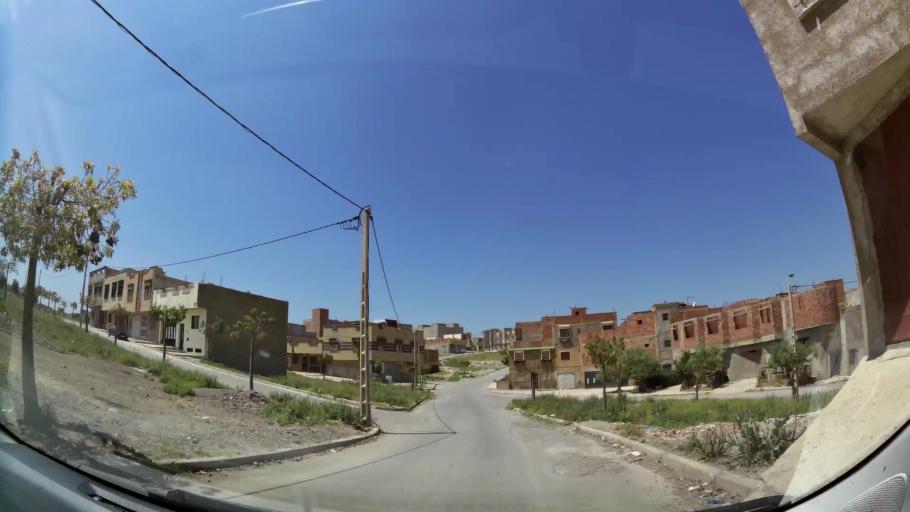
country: MA
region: Oriental
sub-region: Oujda-Angad
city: Oujda
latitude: 34.6799
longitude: -1.9504
